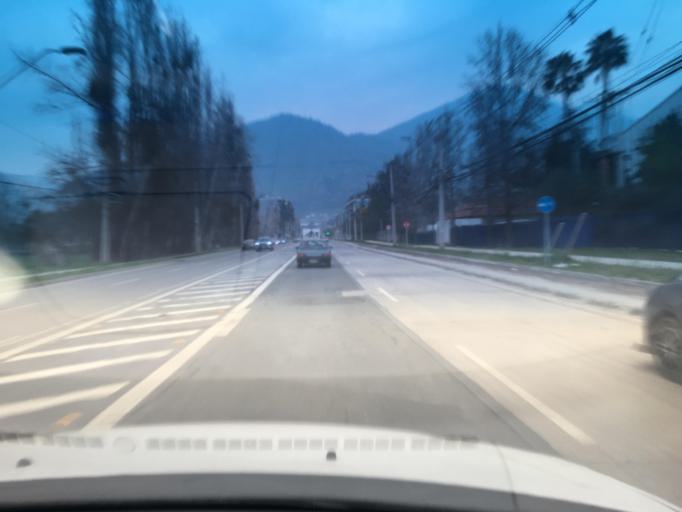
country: CL
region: Santiago Metropolitan
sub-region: Provincia de Santiago
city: Santiago
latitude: -33.3898
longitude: -70.6238
